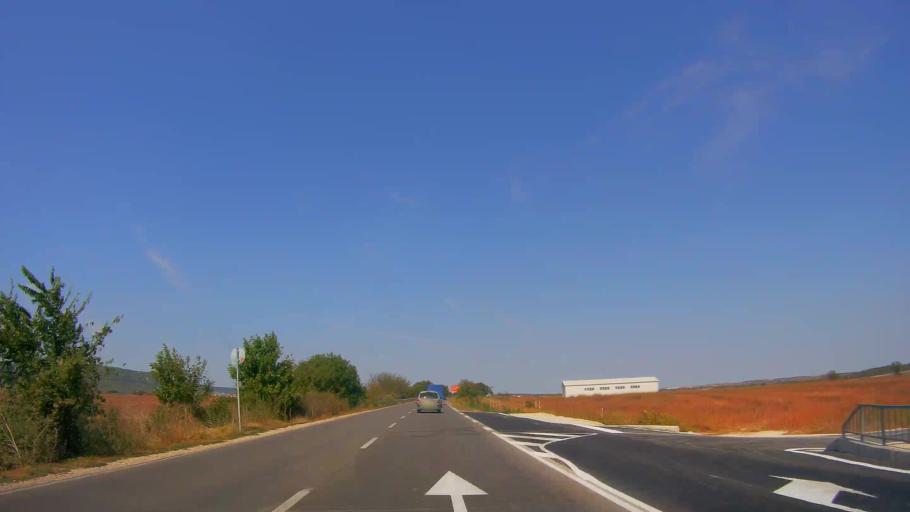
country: BG
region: Shumen
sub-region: Obshtina Shumen
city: Shumen
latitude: 43.2334
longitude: 26.9845
